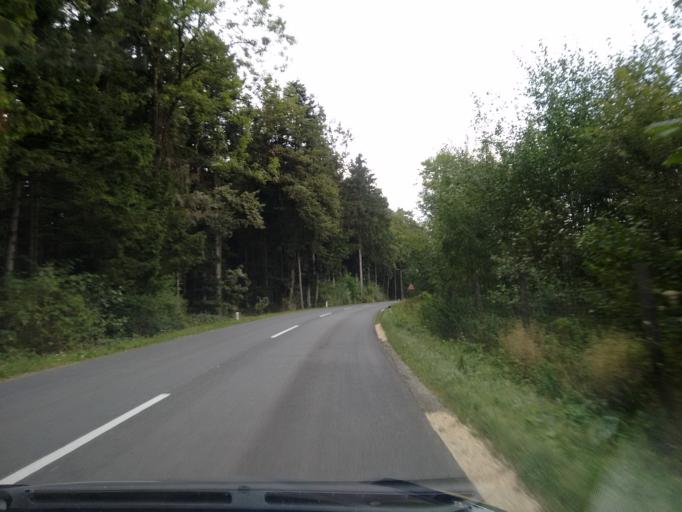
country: AT
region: Upper Austria
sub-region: Wels-Land
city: Marchtrenk
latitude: 48.1557
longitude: 14.1527
